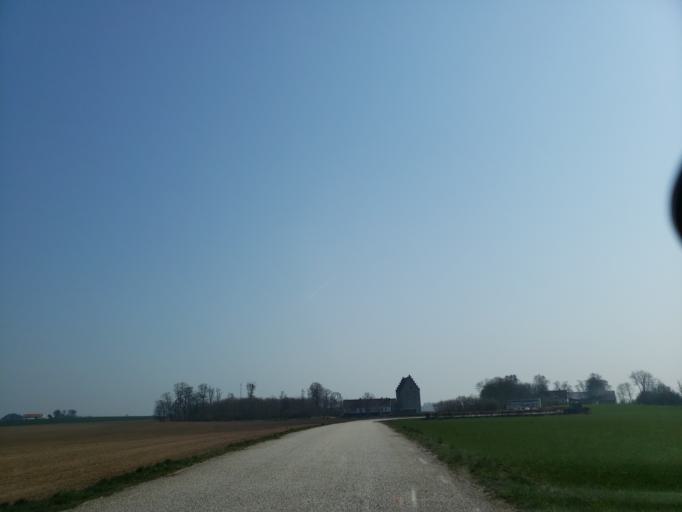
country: SE
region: Skane
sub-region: Simrishamns Kommun
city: Simrishamn
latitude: 55.5022
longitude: 14.2248
